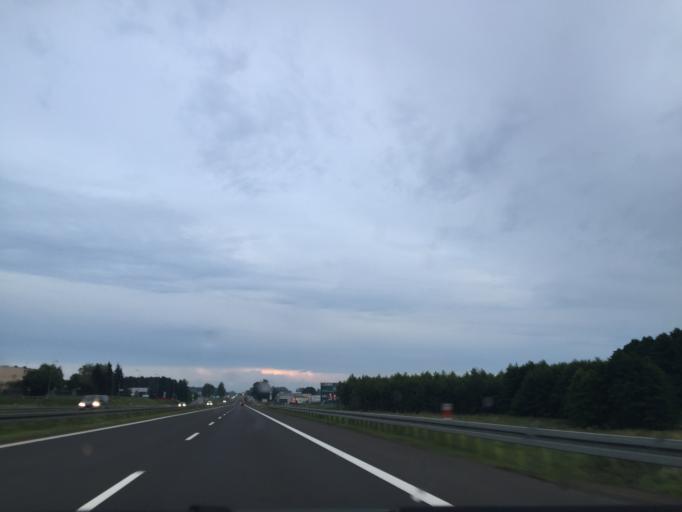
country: PL
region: Podlasie
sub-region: Powiat bialostocki
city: Choroszcz
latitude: 53.1548
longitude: 23.0238
